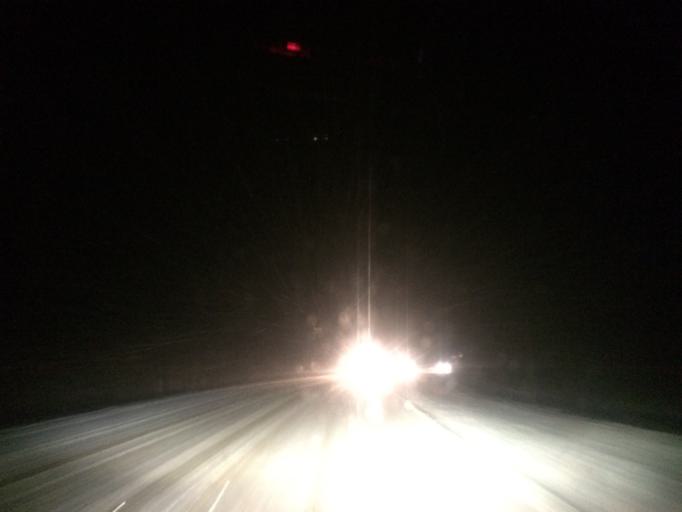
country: RU
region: Tula
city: Dubna
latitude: 54.0865
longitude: 37.0595
